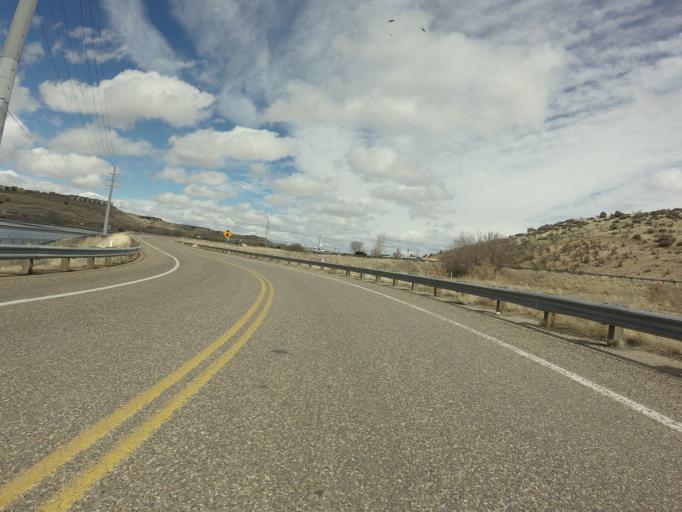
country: US
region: Arizona
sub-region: Yavapai County
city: Prescott
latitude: 34.5721
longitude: -112.4286
